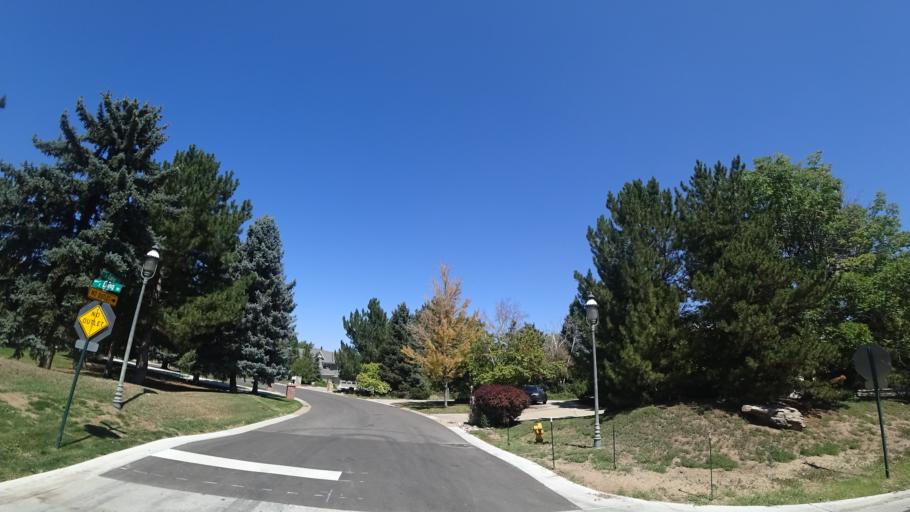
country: US
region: Colorado
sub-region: Arapahoe County
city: Greenwood Village
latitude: 39.6115
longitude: -104.9565
